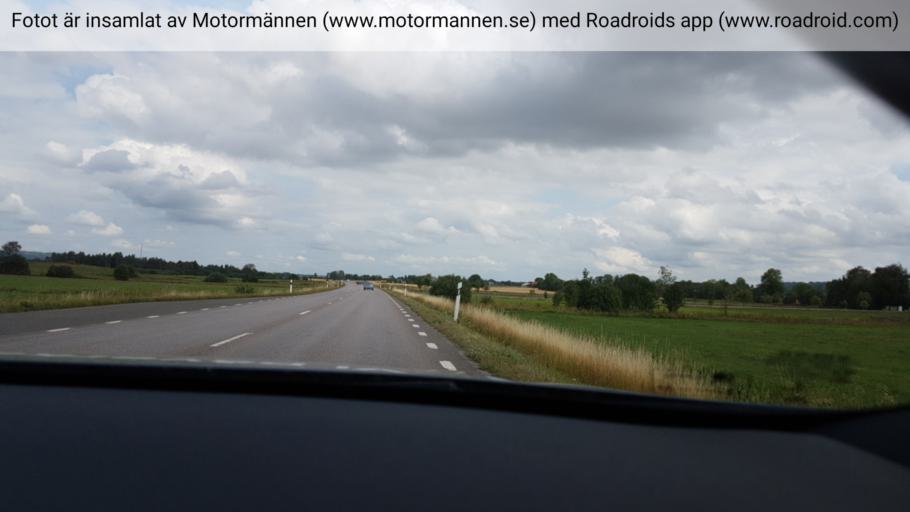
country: SE
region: Vaestra Goetaland
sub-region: Falkopings Kommun
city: Falkoeping
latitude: 58.1127
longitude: 13.5417
